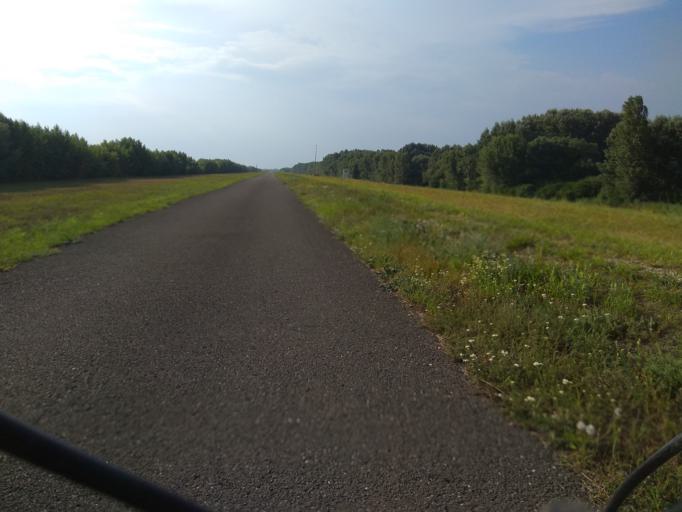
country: SK
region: Trnavsky
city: Gabcikovo
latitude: 47.8447
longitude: 17.5843
